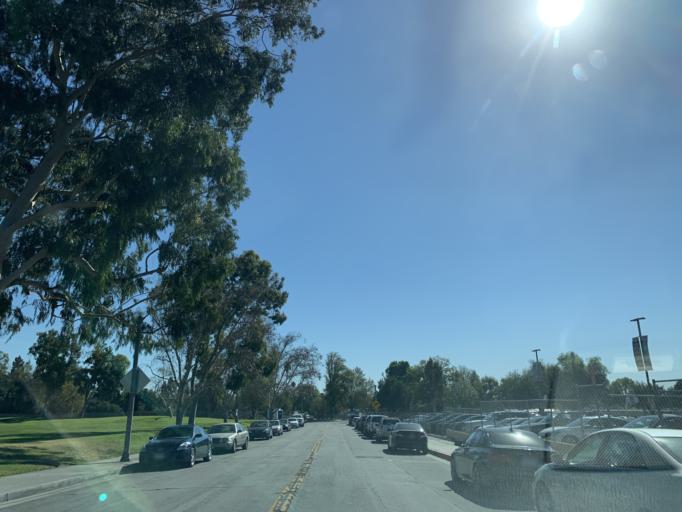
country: US
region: California
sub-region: Orange County
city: Placentia
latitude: 33.8840
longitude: -117.8964
